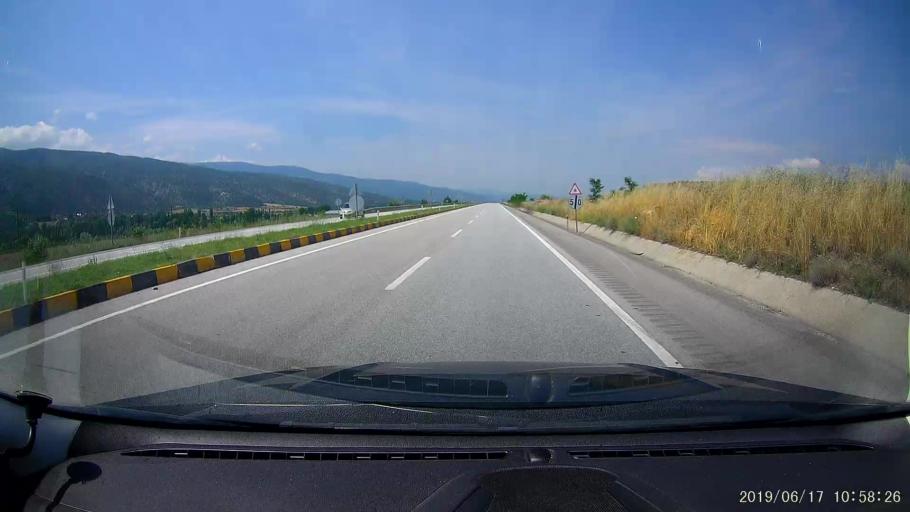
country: TR
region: Kastamonu
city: Tosya
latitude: 41.0433
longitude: 34.2246
